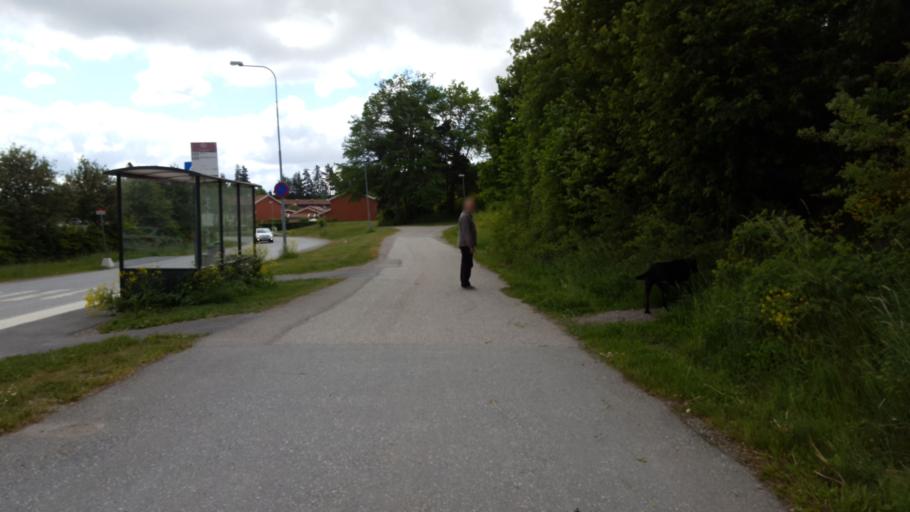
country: SE
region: Stockholm
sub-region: Upplands Vasby Kommun
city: Upplands Vaesby
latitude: 59.5147
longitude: 17.8866
